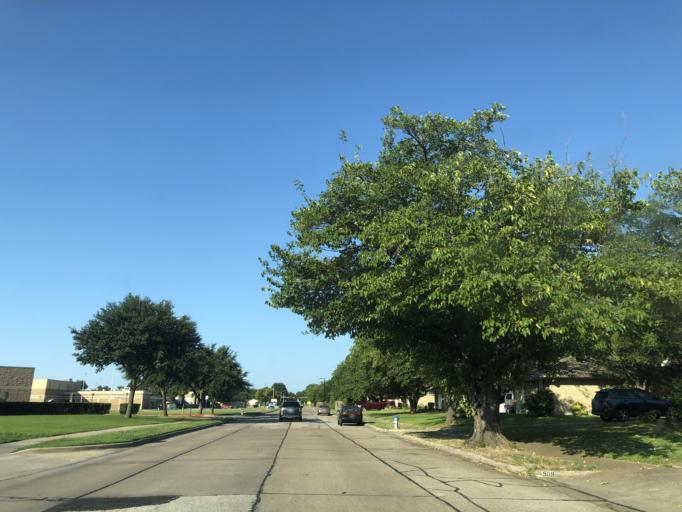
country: US
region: Texas
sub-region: Dallas County
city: Garland
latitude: 32.8586
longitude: -96.6337
